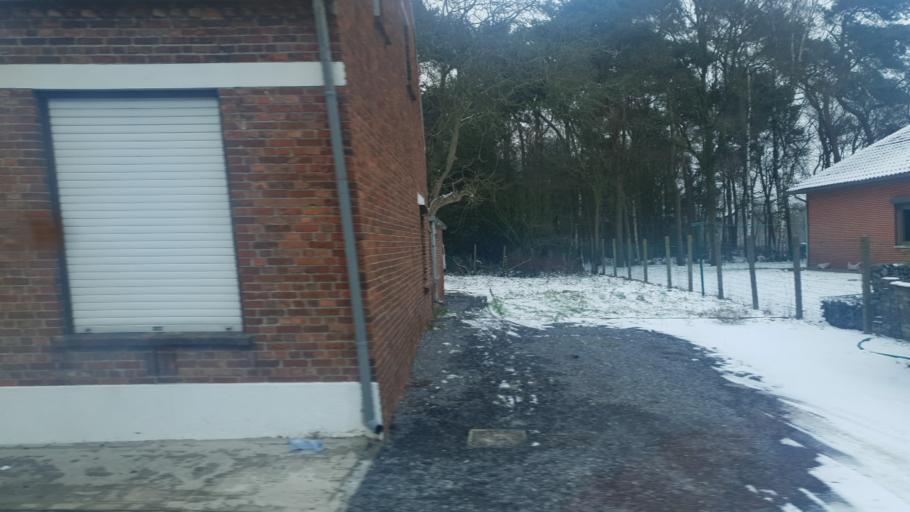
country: BE
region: Flanders
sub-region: Provincie Limburg
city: Overpelt
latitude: 51.2000
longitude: 5.4293
